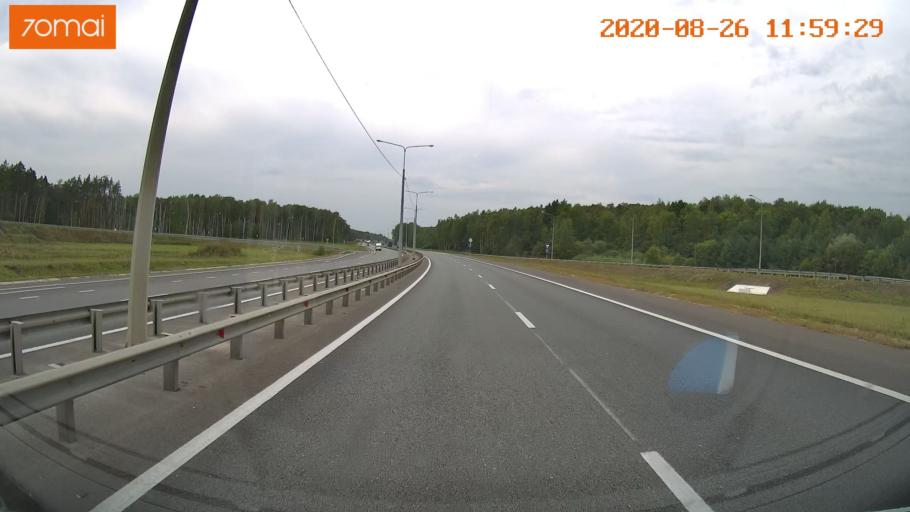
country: RU
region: Rjazan
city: Kiritsy
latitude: 54.2859
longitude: 40.2986
